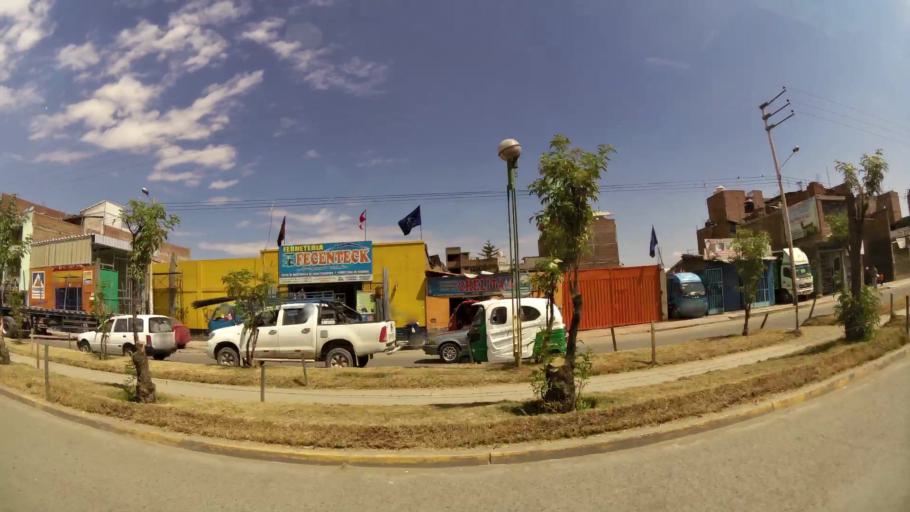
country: PE
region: Junin
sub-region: Provincia de Huancayo
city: Huancayo
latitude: -12.0737
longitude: -75.2028
